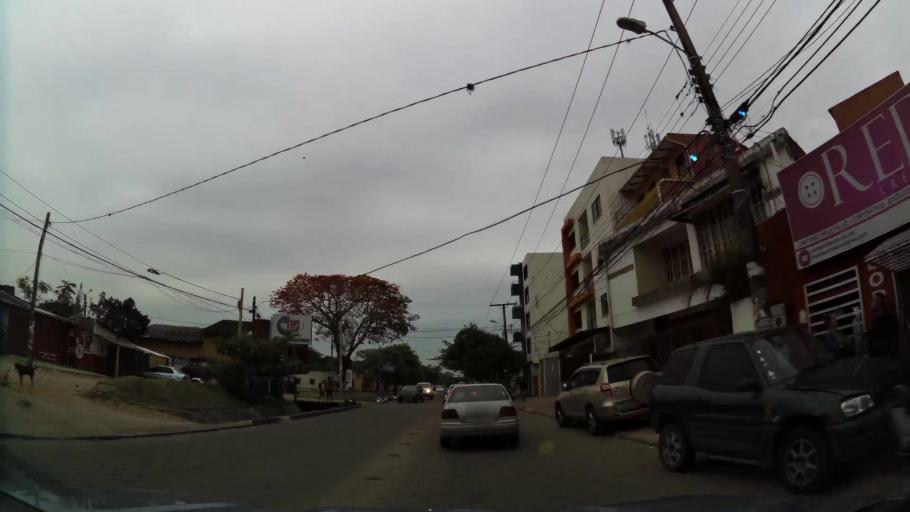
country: BO
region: Santa Cruz
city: Santa Cruz de la Sierra
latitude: -17.7788
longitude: -63.1973
